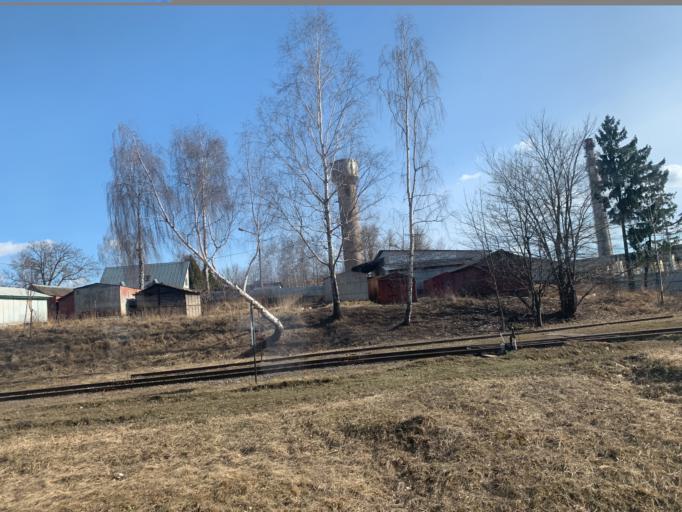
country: BY
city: Fanipol
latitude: 53.7416
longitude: 27.3267
